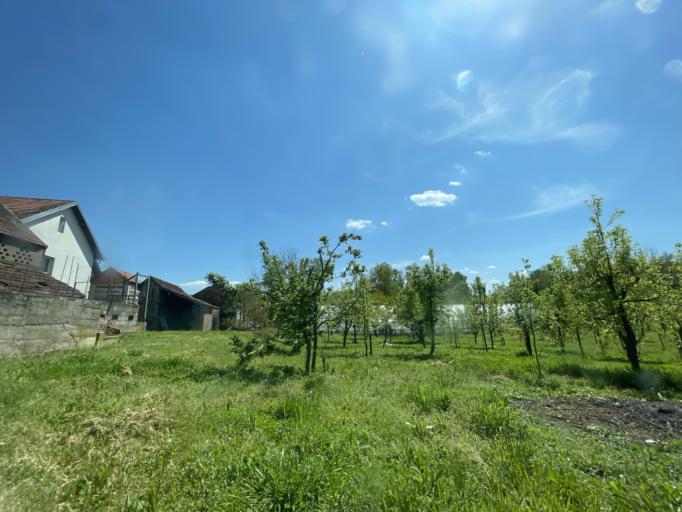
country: BA
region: Federation of Bosnia and Herzegovina
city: Donja Dubica
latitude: 45.0311
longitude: 18.4126
